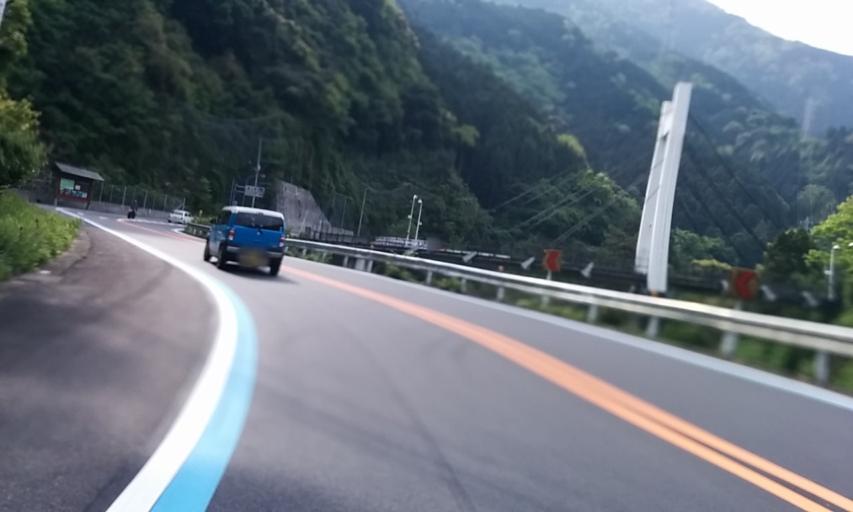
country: JP
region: Ehime
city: Niihama
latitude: 33.9040
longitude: 133.3101
